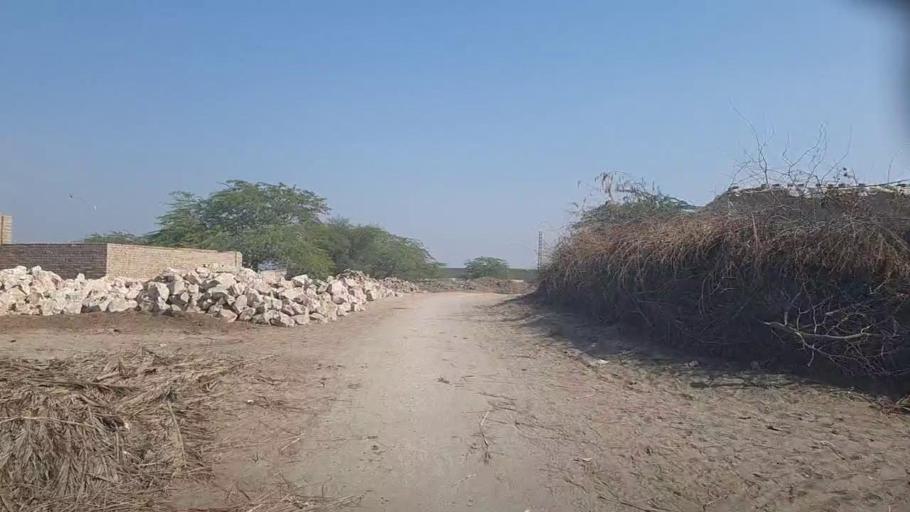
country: PK
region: Sindh
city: Kot Diji
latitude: 27.4316
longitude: 68.7239
